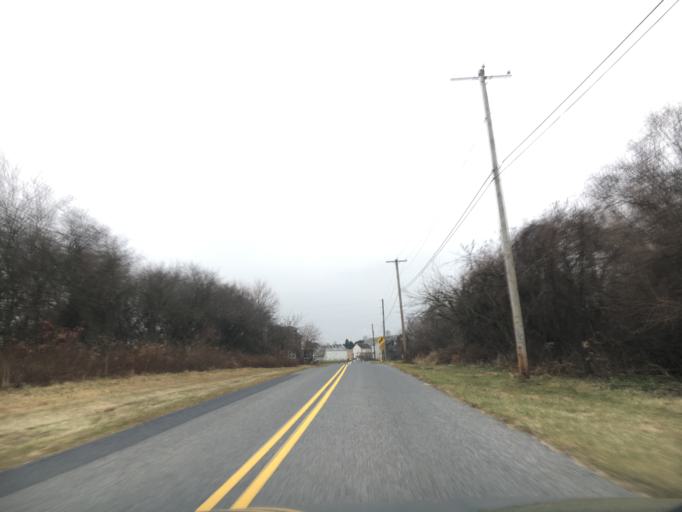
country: US
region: Pennsylvania
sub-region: Lehigh County
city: Schnecksville
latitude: 40.6938
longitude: -75.5821
